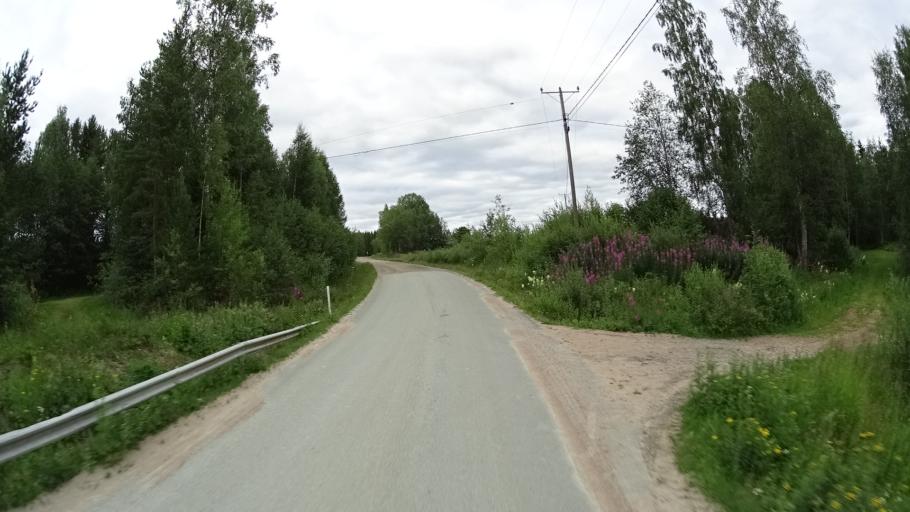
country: FI
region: Satakunta
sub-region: Pohjois-Satakunta
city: Jaemijaervi
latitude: 61.7682
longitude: 22.8316
